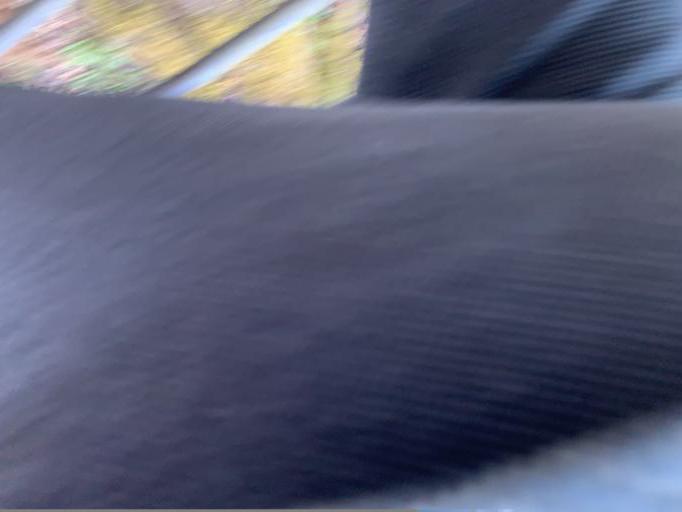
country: JP
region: Miyagi
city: Sendai
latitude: 38.2542
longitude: 140.8558
